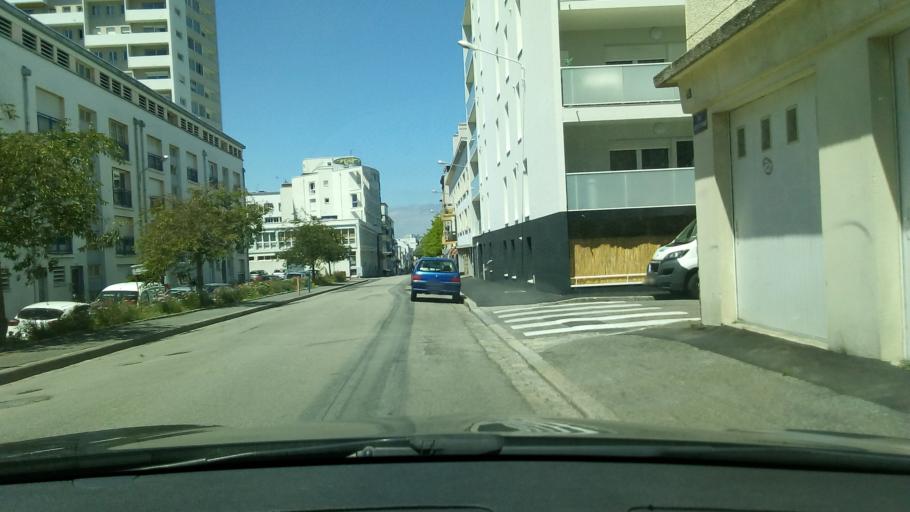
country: FR
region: Brittany
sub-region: Departement du Morbihan
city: Lorient
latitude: 47.7469
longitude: -3.3568
